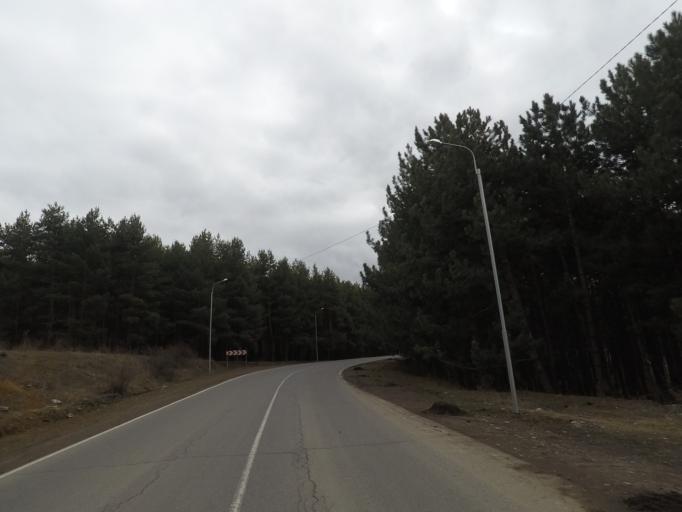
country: GE
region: Samtskhe-Javakheti
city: Aspindza
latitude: 41.5824
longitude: 43.2448
